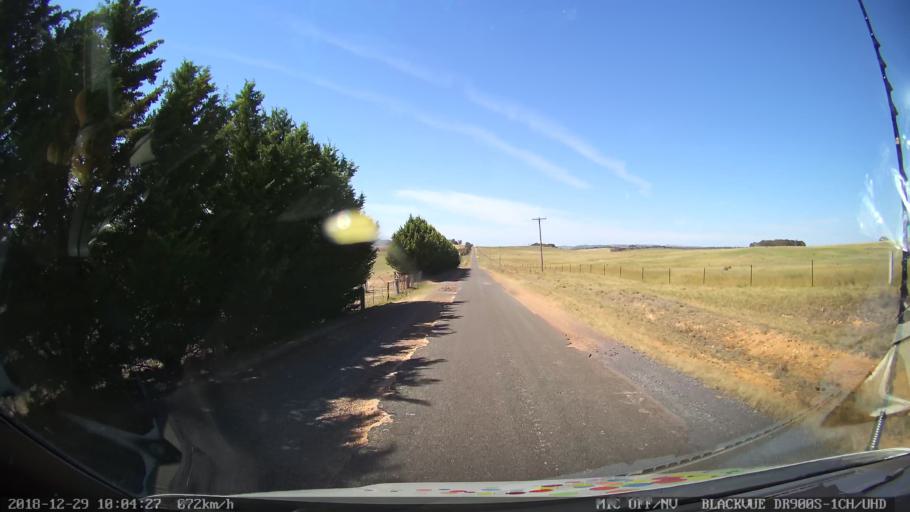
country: AU
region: New South Wales
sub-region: Goulburn Mulwaree
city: Goulburn
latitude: -34.8222
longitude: 149.4553
